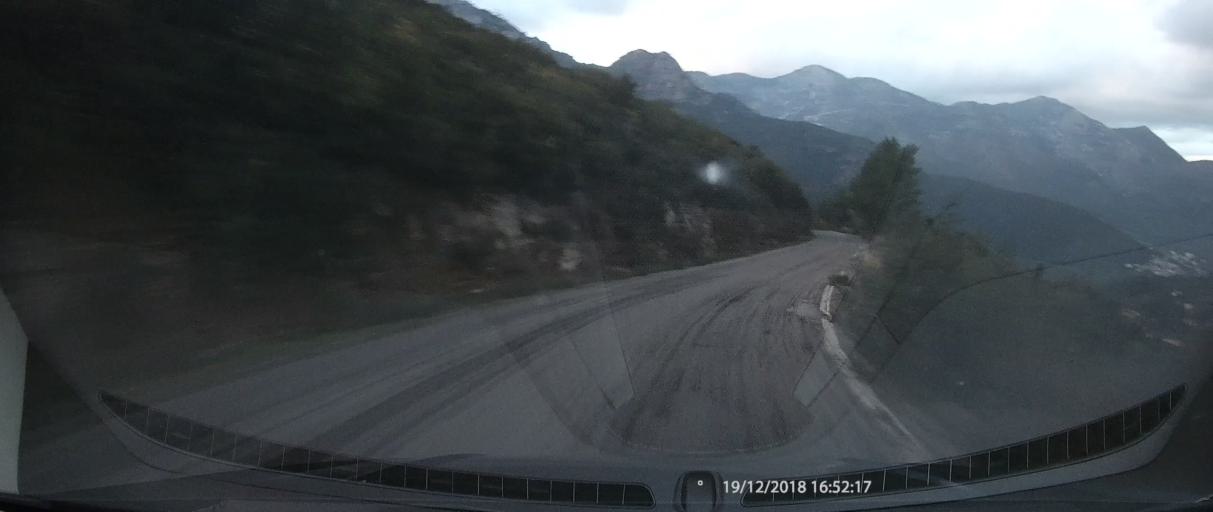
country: GR
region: Peloponnese
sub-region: Nomos Lakonias
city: Sykea
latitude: 36.9559
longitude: 22.9913
